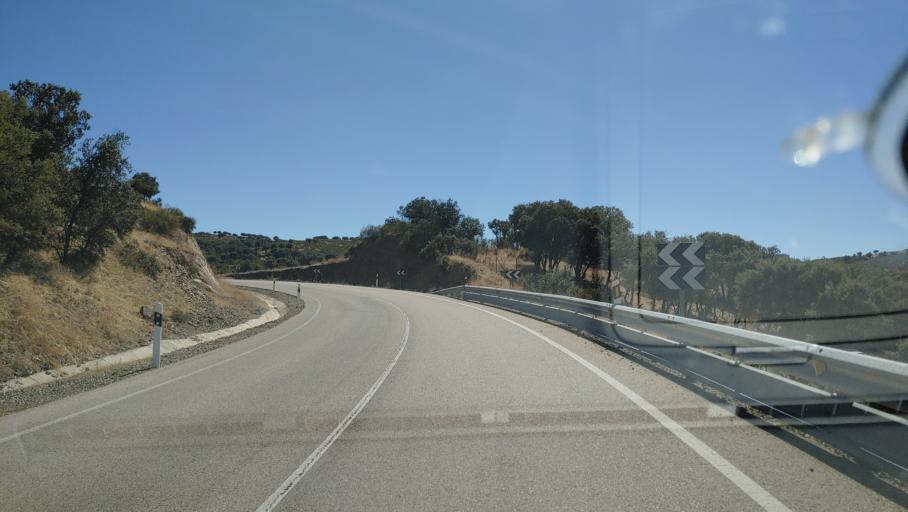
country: ES
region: Andalusia
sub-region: Provincia de Jaen
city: Genave
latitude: 38.5016
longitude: -2.7774
